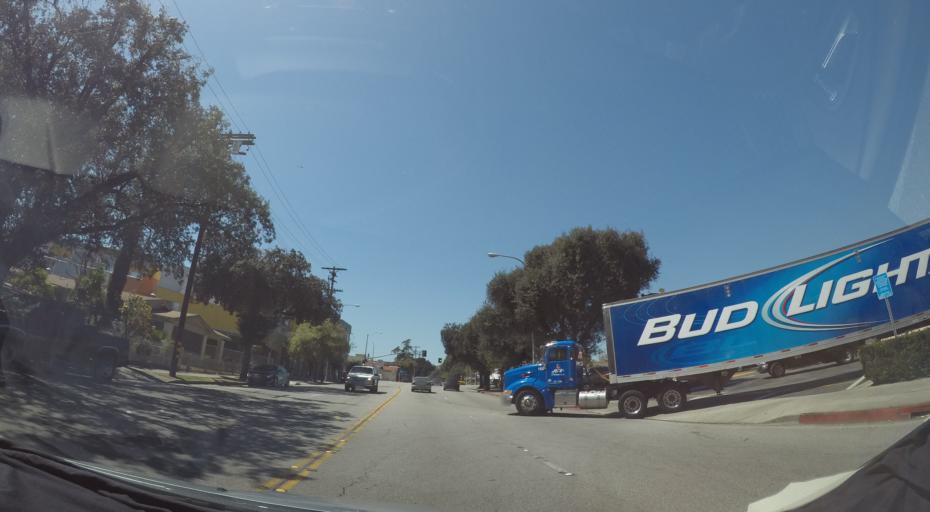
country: US
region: California
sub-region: Los Angeles County
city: Pasadena
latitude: 34.1578
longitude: -118.1404
